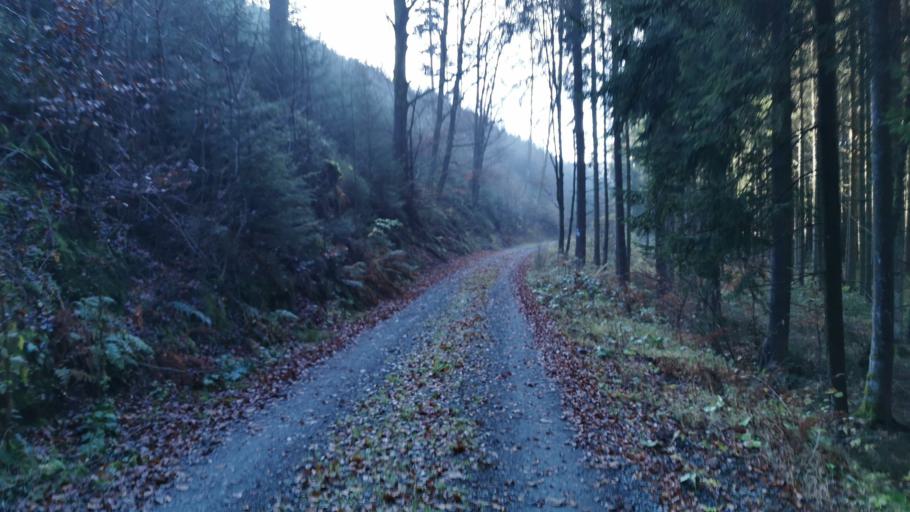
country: DE
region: Bavaria
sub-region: Upper Franconia
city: Tschirn
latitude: 50.4170
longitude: 11.4436
